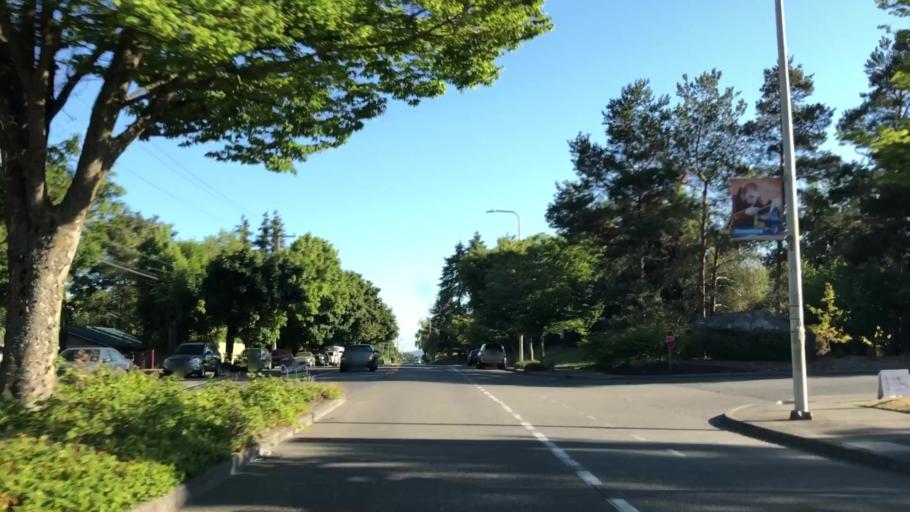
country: US
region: Washington
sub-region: King County
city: White Center
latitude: 47.5506
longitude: -122.3548
